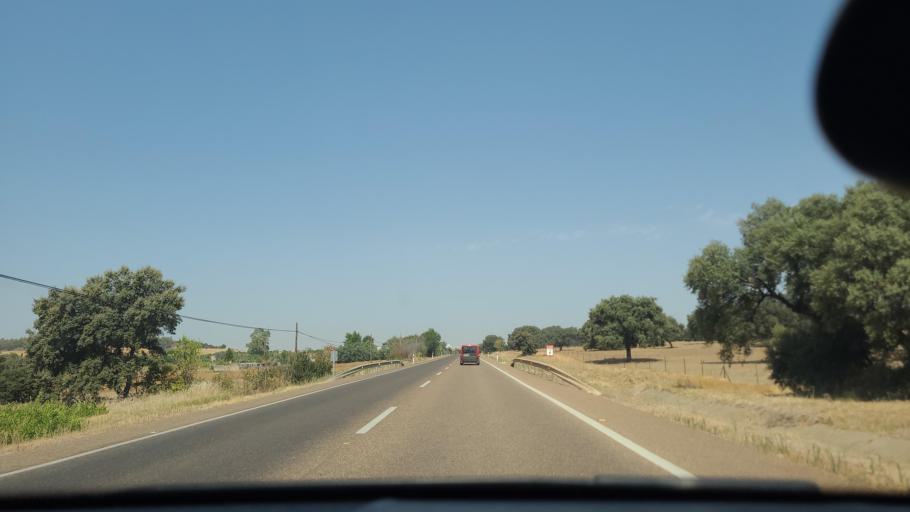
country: ES
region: Extremadura
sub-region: Provincia de Badajoz
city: Badajoz
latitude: 38.8380
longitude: -6.9261
